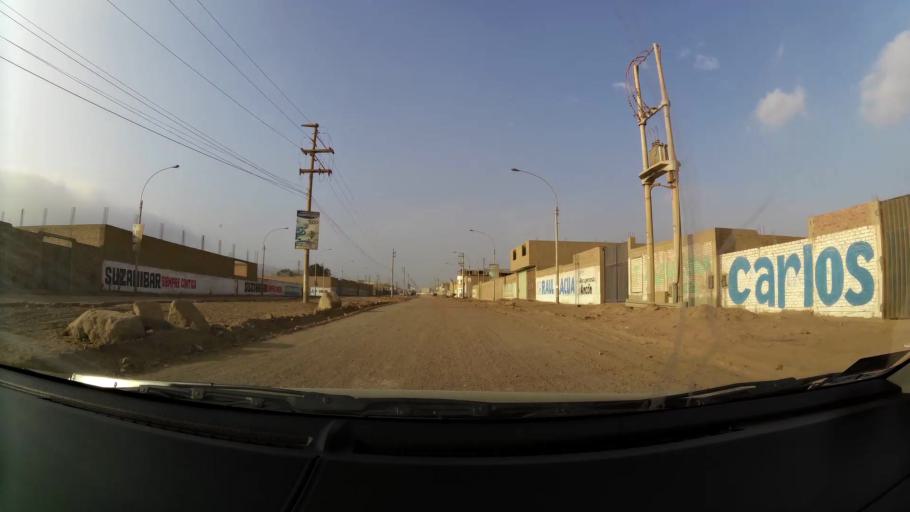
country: PE
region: Lima
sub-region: Lima
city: Santa Rosa
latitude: -11.7591
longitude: -77.1578
